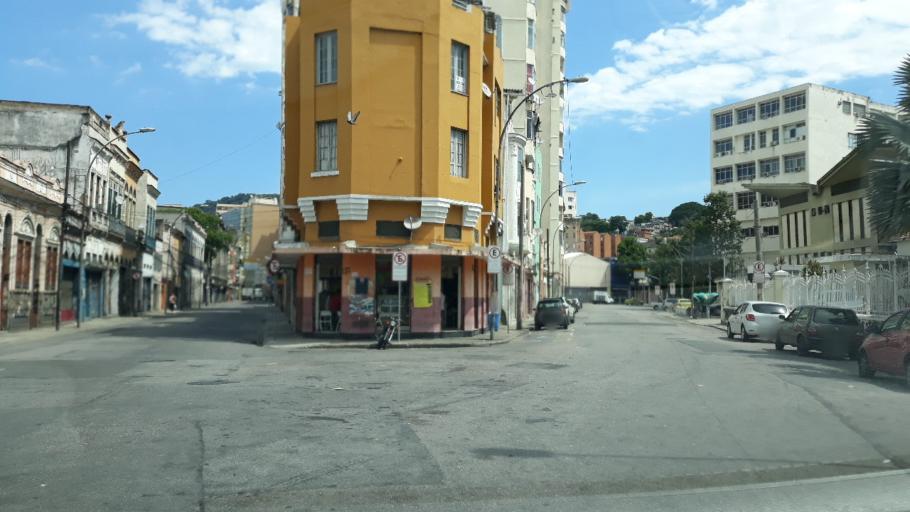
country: BR
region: Rio de Janeiro
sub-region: Rio De Janeiro
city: Rio de Janeiro
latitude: -22.9090
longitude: -43.1919
